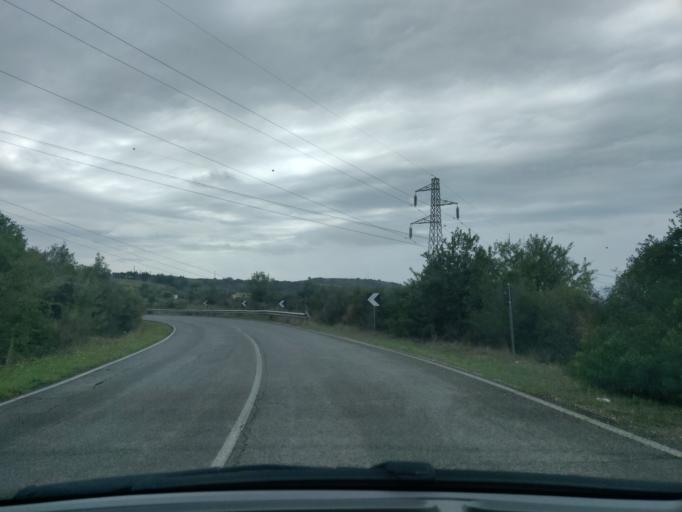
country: IT
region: Latium
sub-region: Citta metropolitana di Roma Capitale
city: Allumiere
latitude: 42.1235
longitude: 11.8632
